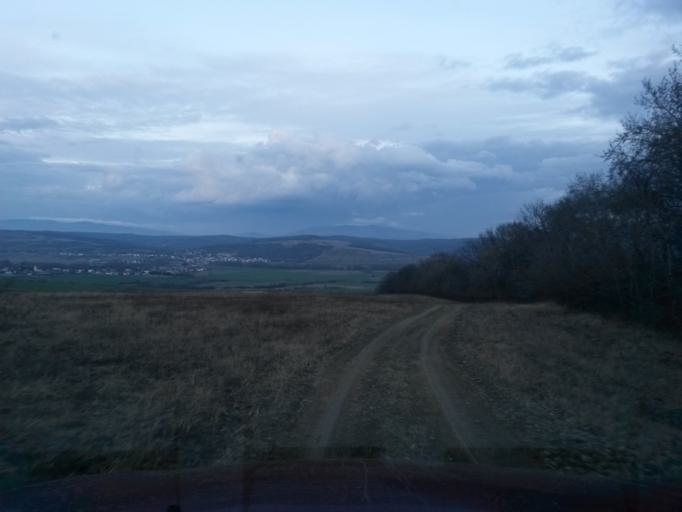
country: SK
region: Kosicky
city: Kosice
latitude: 48.6998
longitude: 21.3100
